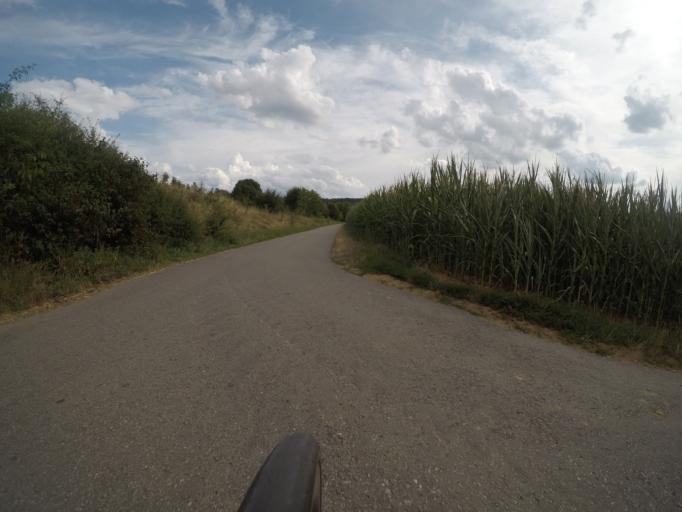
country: DE
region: Baden-Wuerttemberg
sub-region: Regierungsbezirk Stuttgart
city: Weil der Stadt
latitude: 48.7333
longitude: 8.8837
